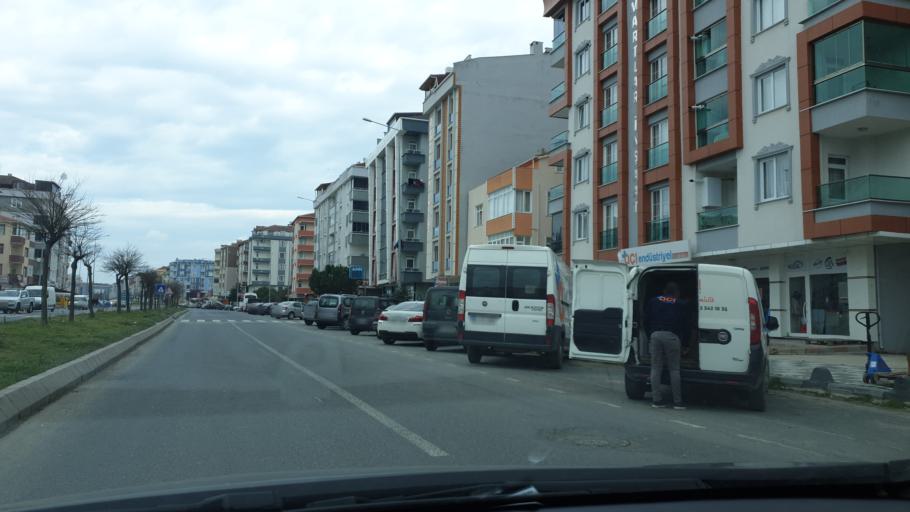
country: TR
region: Tekirdag
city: Cerkezkoey
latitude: 41.2859
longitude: 27.9882
